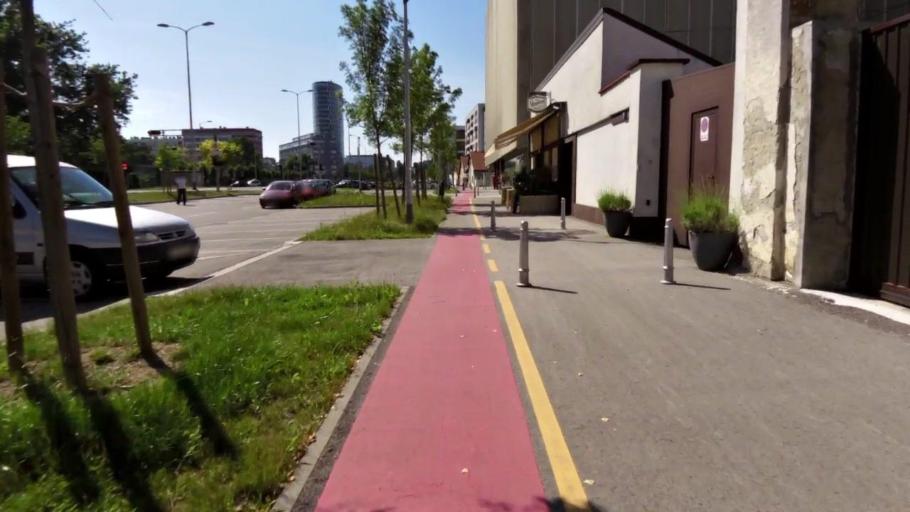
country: HR
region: Grad Zagreb
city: Novi Zagreb
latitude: 45.7999
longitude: 16.0124
